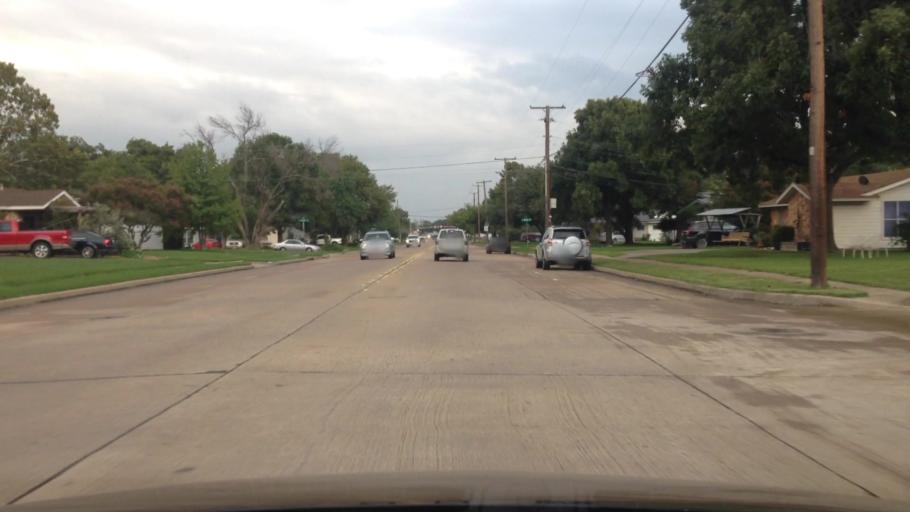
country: US
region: Texas
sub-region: Johnson County
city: Burleson
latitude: 32.5485
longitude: -97.3314
